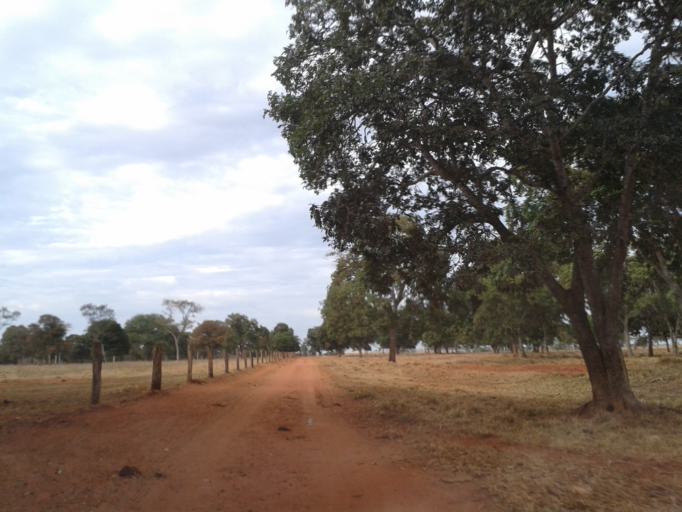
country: BR
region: Minas Gerais
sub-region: Santa Vitoria
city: Santa Vitoria
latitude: -18.7533
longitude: -50.1953
